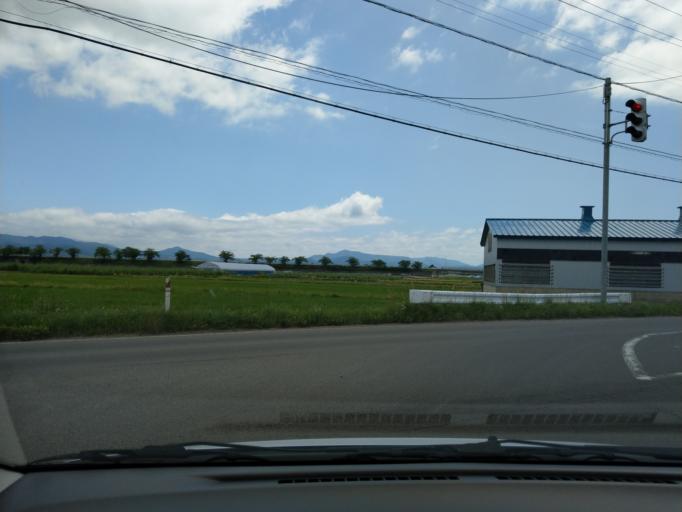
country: JP
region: Aomori
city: Kuroishi
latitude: 40.6364
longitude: 140.5676
